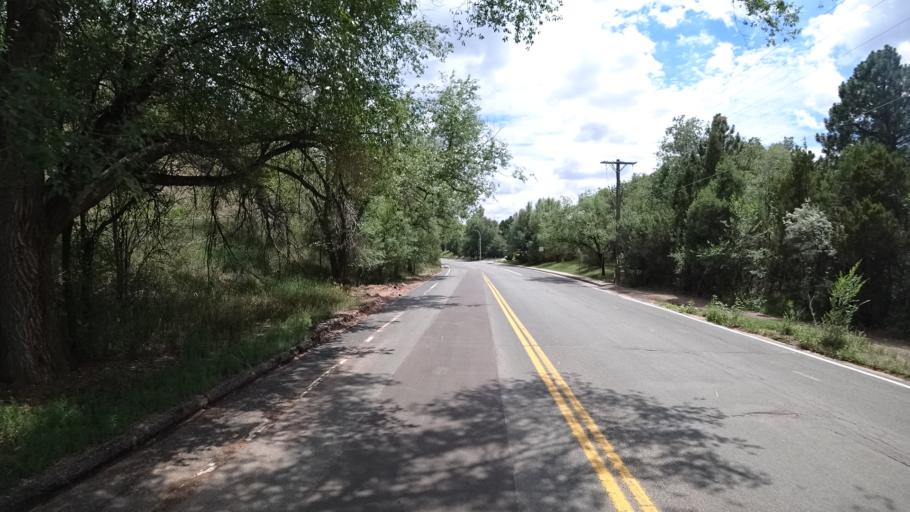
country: US
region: Colorado
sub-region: El Paso County
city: Colorado Springs
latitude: 38.8511
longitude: -104.8409
